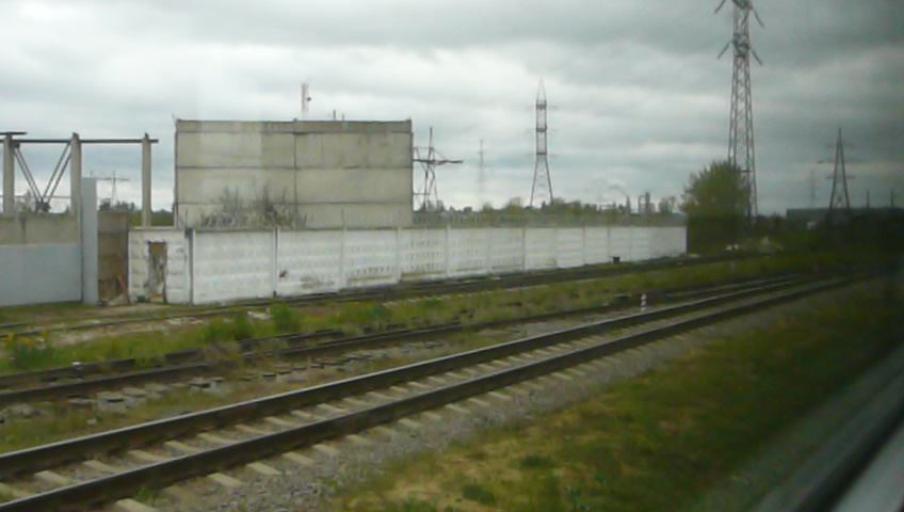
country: RU
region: Moskovskaya
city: Yegor'yevsk
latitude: 55.3958
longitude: 39.0044
